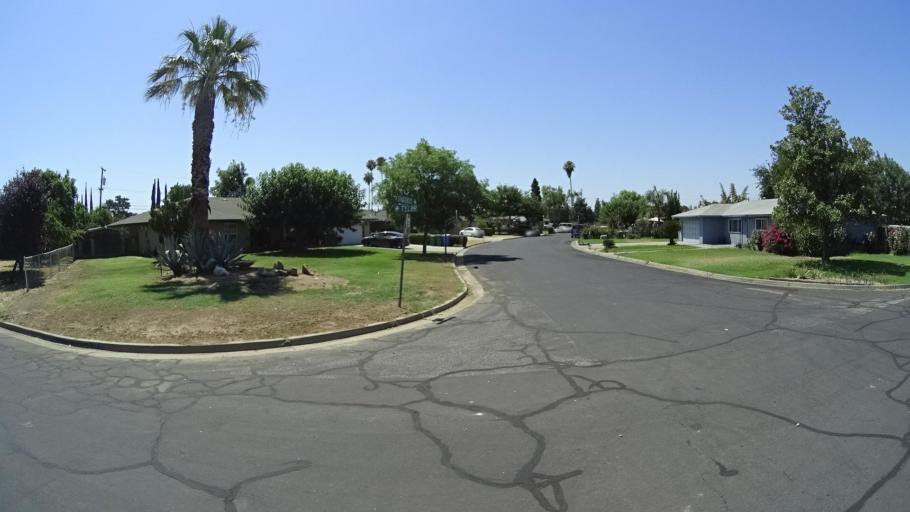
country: US
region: California
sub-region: Fresno County
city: Sunnyside
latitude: 36.7552
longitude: -119.7128
